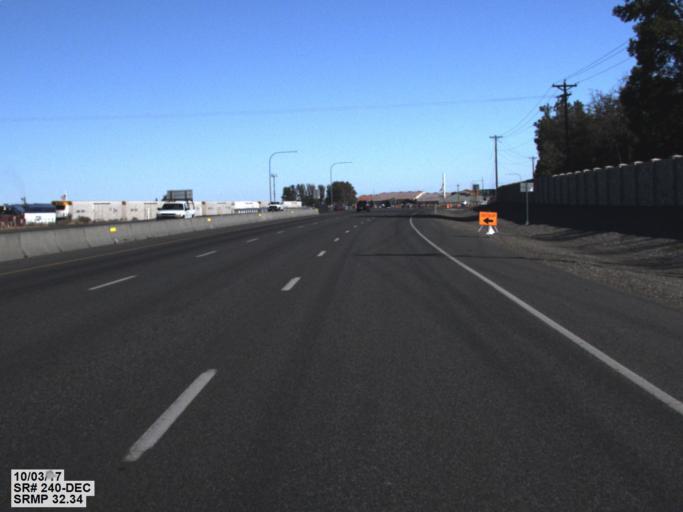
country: US
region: Washington
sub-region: Benton County
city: Richland
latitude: 46.2887
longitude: -119.3063
